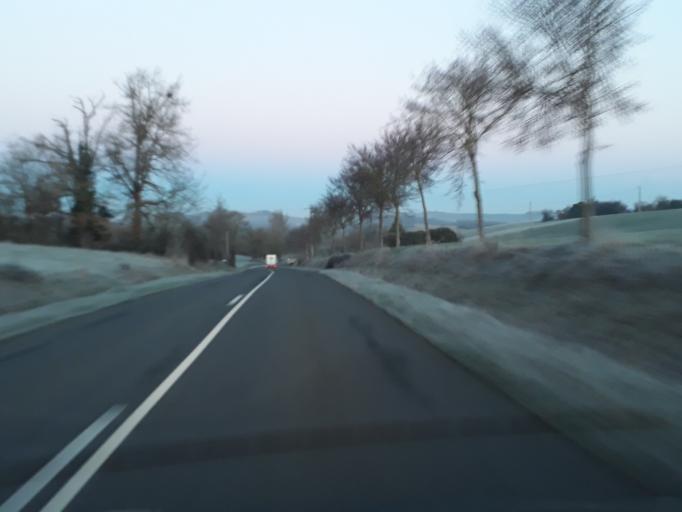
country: FR
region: Midi-Pyrenees
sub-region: Departement du Gers
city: Samatan
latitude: 43.5029
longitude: 0.9041
